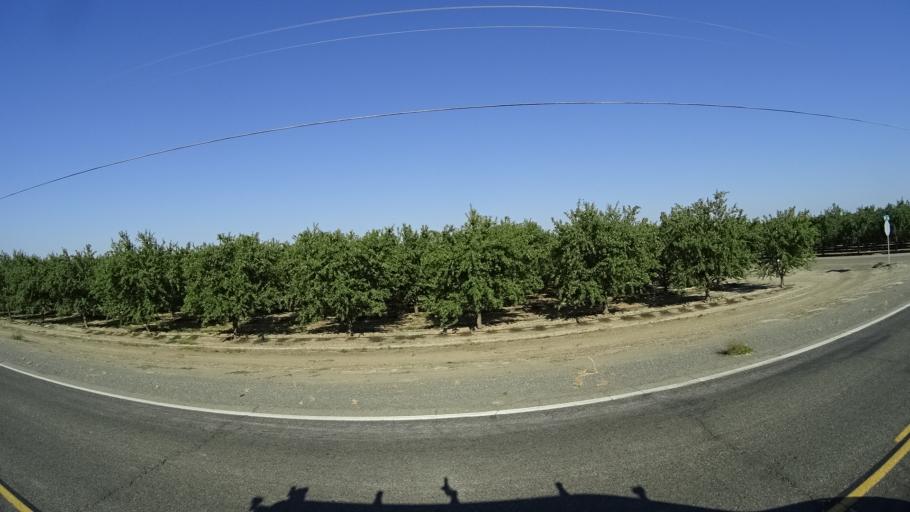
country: US
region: California
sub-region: Kings County
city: Lucerne
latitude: 36.3912
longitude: -119.7090
